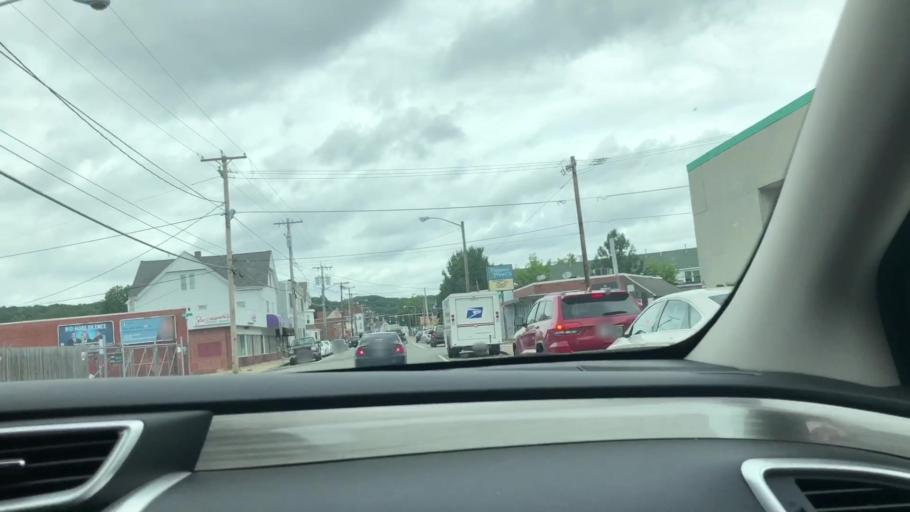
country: US
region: Rhode Island
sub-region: Providence County
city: Central Falls
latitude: 41.8769
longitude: -71.4149
